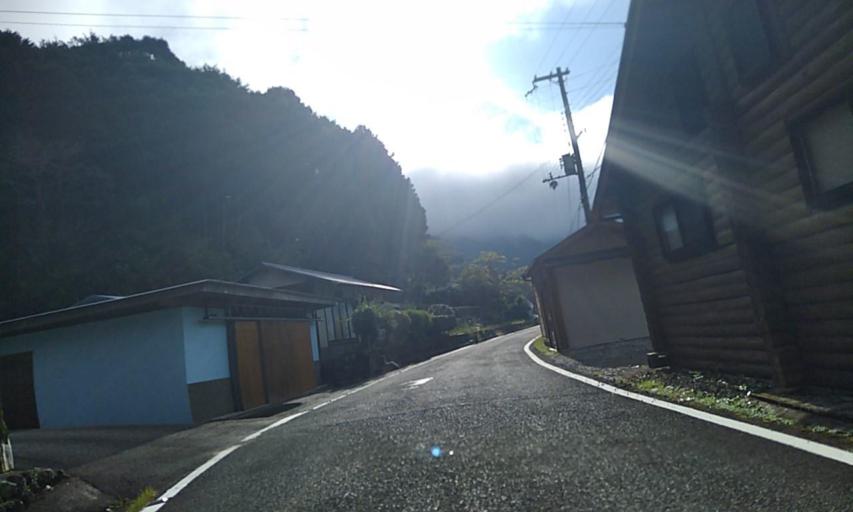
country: JP
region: Wakayama
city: Shingu
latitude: 33.9272
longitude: 135.9810
